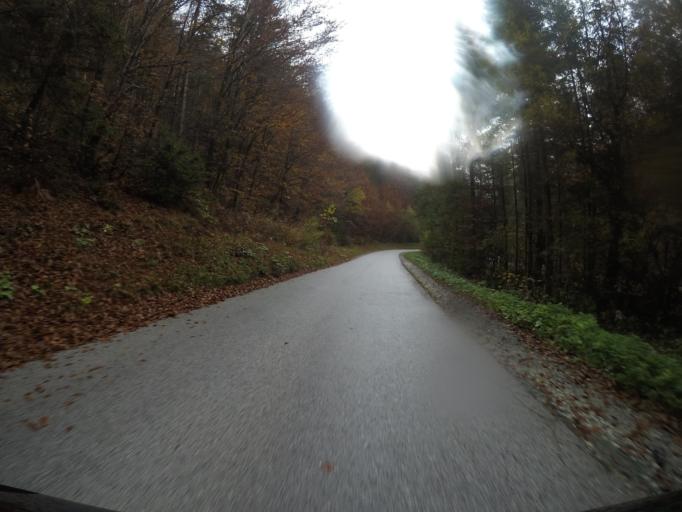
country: SI
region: Kranjska Gora
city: Mojstrana
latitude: 46.4487
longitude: 13.9219
